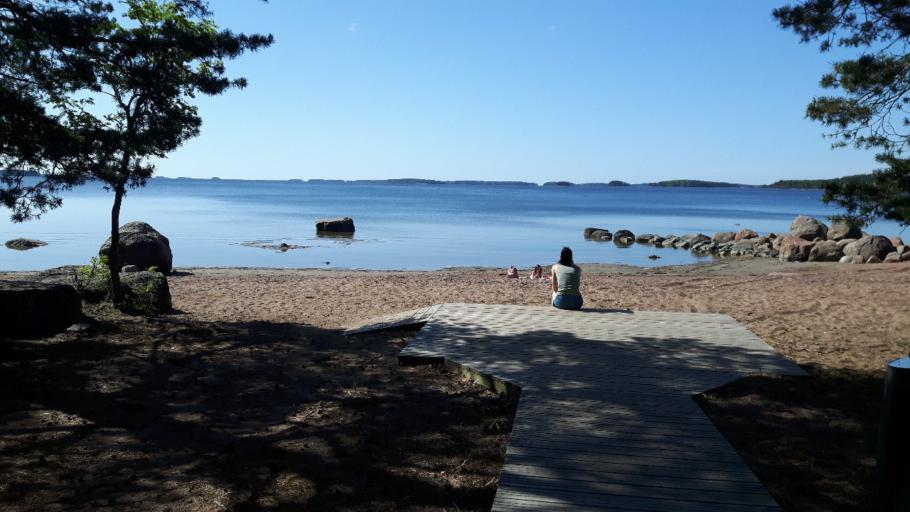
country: FI
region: Kymenlaakso
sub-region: Kotka-Hamina
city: Hamina
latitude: 60.5260
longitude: 27.2516
